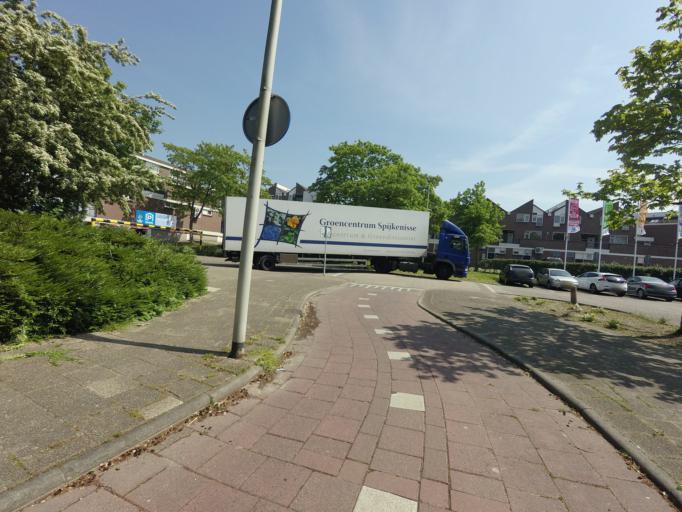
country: NL
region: South Holland
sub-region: Gemeente Hellevoetsluis
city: Hellevoetsluis
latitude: 51.8318
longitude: 4.1456
